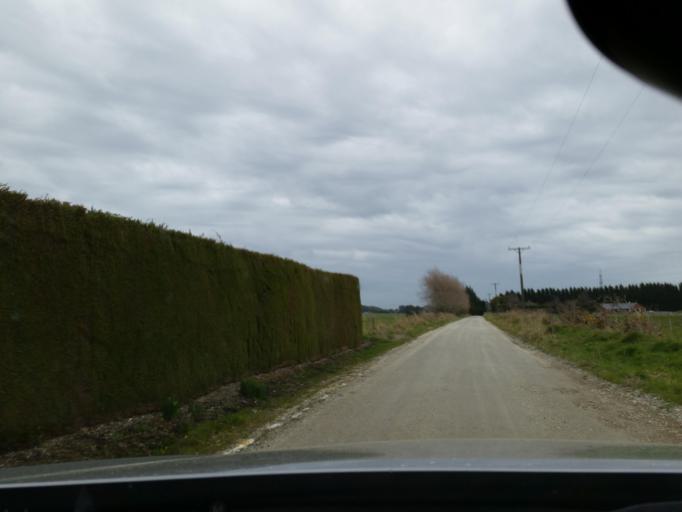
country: NZ
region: Southland
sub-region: Invercargill City
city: Invercargill
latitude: -46.2951
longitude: 168.4793
